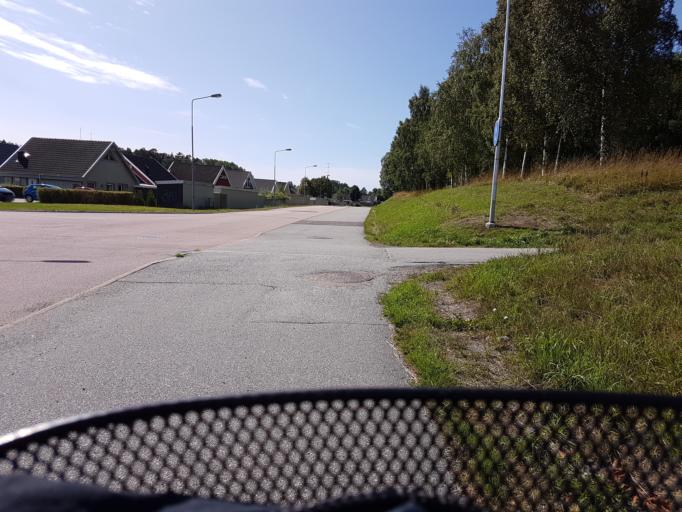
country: SE
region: Vaestra Goetaland
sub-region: Ale Kommun
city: Alvangen
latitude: 57.9514
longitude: 12.1159
